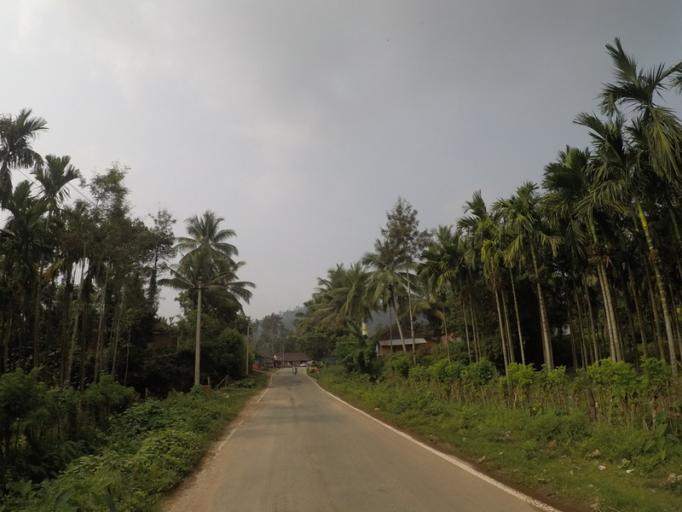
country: IN
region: Karnataka
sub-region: Chikmagalur
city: Mudigere
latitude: 13.2729
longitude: 75.4841
